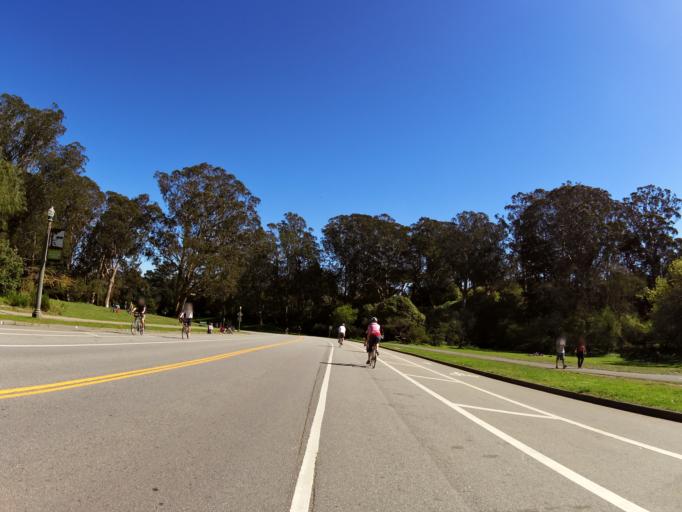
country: US
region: California
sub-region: San Francisco County
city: San Francisco
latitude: 37.7711
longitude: -122.4733
